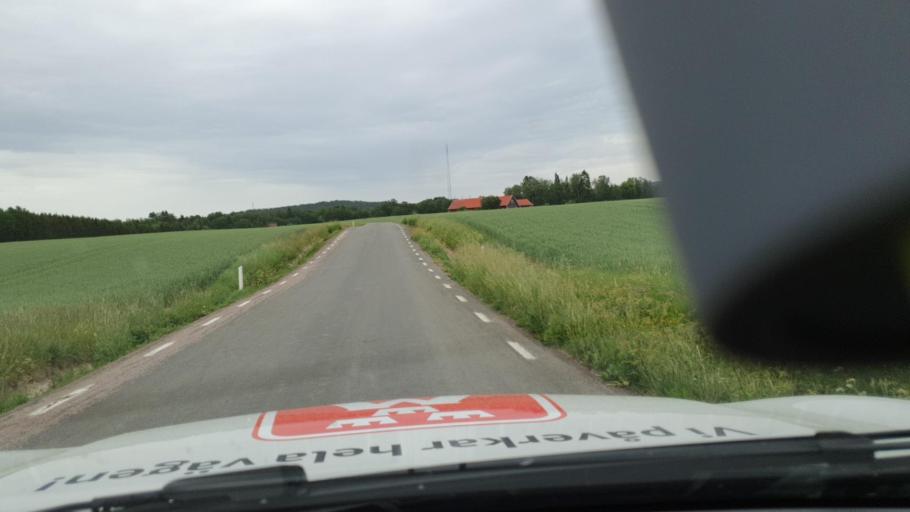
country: SE
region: Vaestra Goetaland
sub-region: Tidaholms Kommun
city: Olofstorp
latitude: 58.3032
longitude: 14.0659
